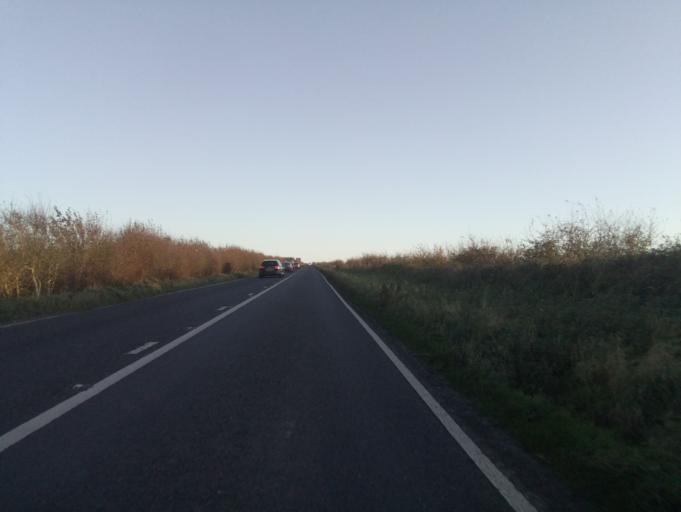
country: GB
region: England
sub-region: Wiltshire
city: Bishopstrow
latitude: 51.1516
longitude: -2.1671
